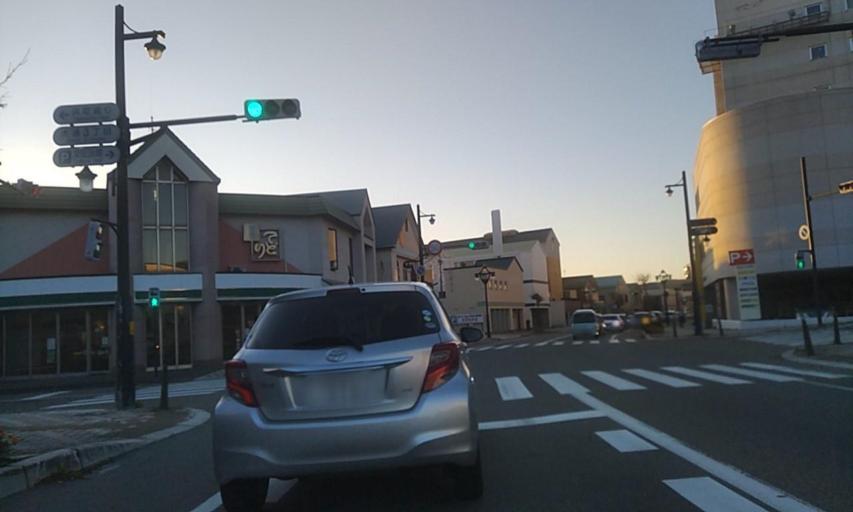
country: JP
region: Hokkaido
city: Shizunai-furukawacho
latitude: 42.1608
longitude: 142.7764
